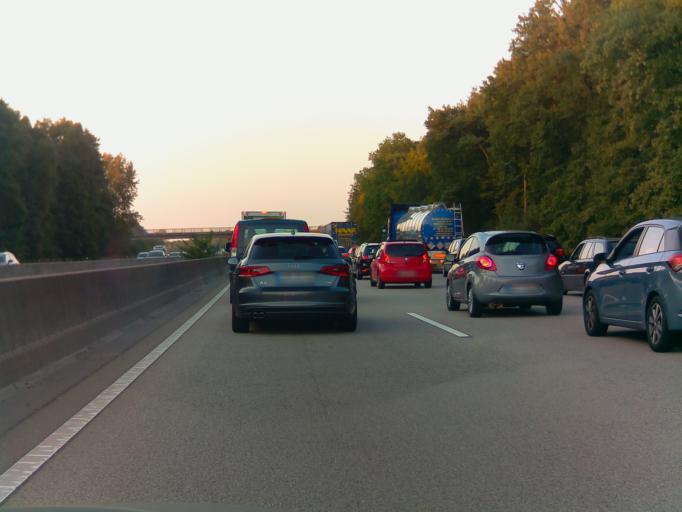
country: DE
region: Hesse
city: Viernheim
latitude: 49.5845
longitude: 8.5607
